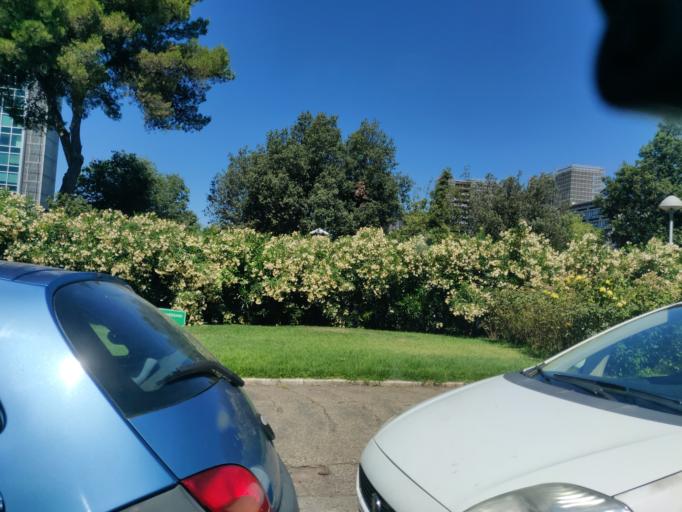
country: IT
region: Latium
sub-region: Citta metropolitana di Roma Capitale
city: Selcetta
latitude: 41.8275
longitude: 12.4731
